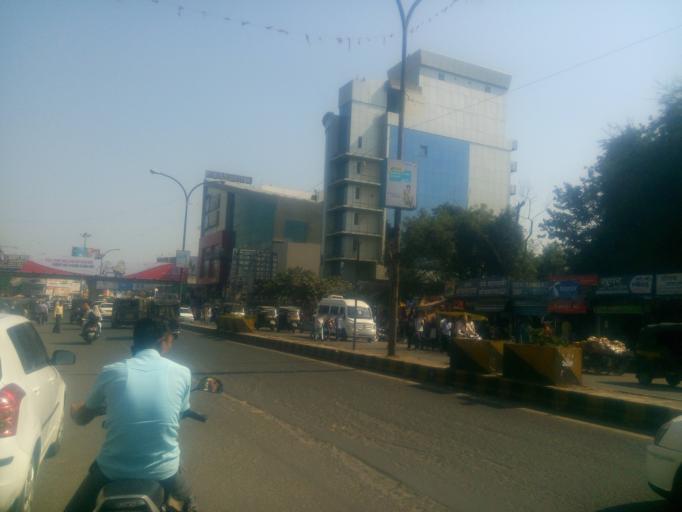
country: IN
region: Maharashtra
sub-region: Nagpur Division
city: Nagpur
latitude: 21.1439
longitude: 79.0792
